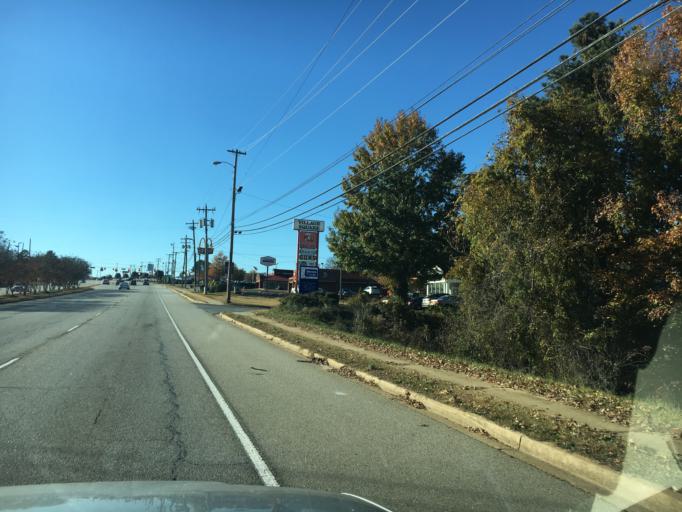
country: US
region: South Carolina
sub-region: Greenville County
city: Greer
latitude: 34.9488
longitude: -82.2322
